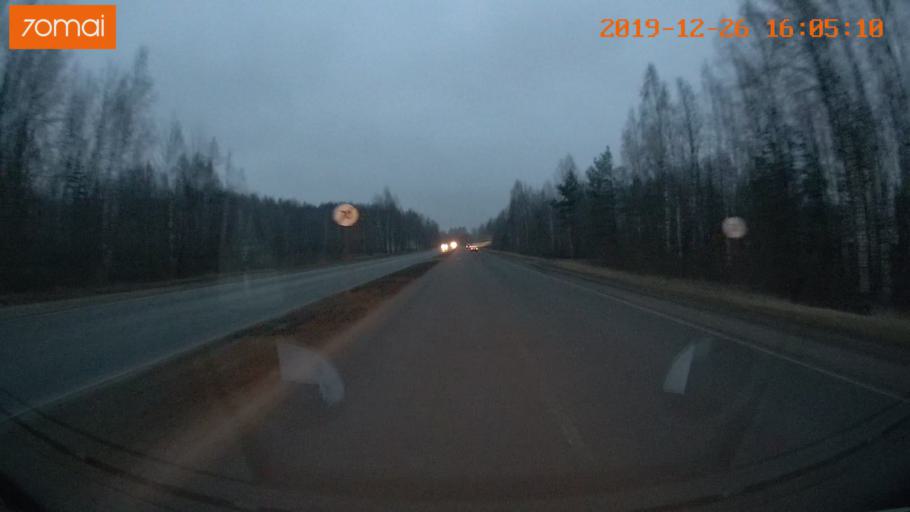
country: RU
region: Jaroslavl
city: Rybinsk
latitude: 58.0068
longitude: 38.8887
